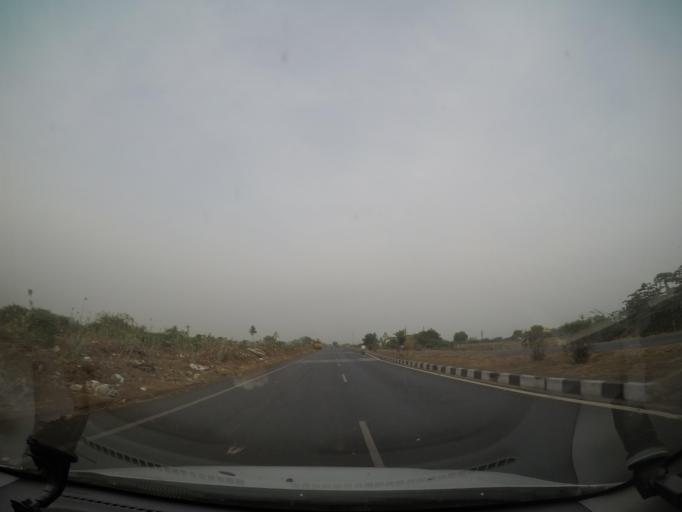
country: IN
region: Andhra Pradesh
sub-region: Krishna
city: Gannavaram
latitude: 16.6311
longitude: 80.9497
